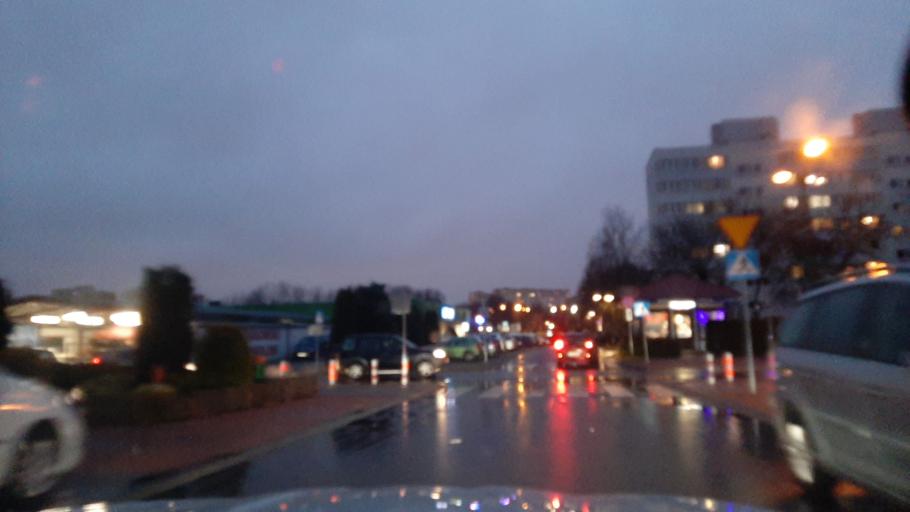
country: PL
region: Lublin Voivodeship
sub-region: Powiat lubelski
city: Lublin
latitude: 51.2691
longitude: 22.5493
